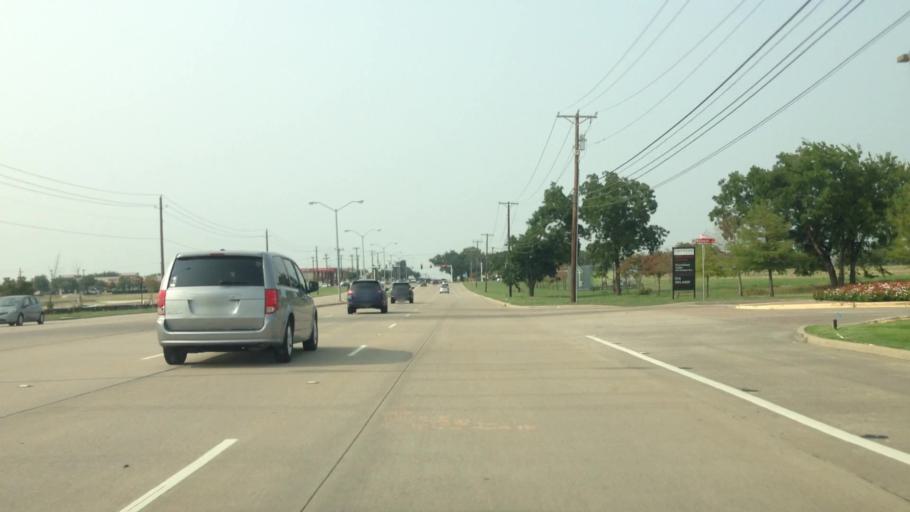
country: US
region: Texas
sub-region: Dallas County
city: Farmers Branch
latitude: 32.9147
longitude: -96.9248
